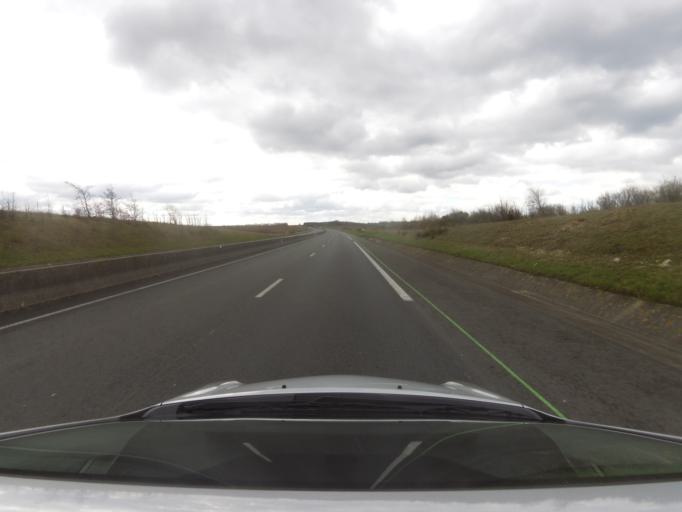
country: FR
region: Nord-Pas-de-Calais
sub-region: Departement du Pas-de-Calais
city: Saint-Josse
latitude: 50.4497
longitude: 1.6945
